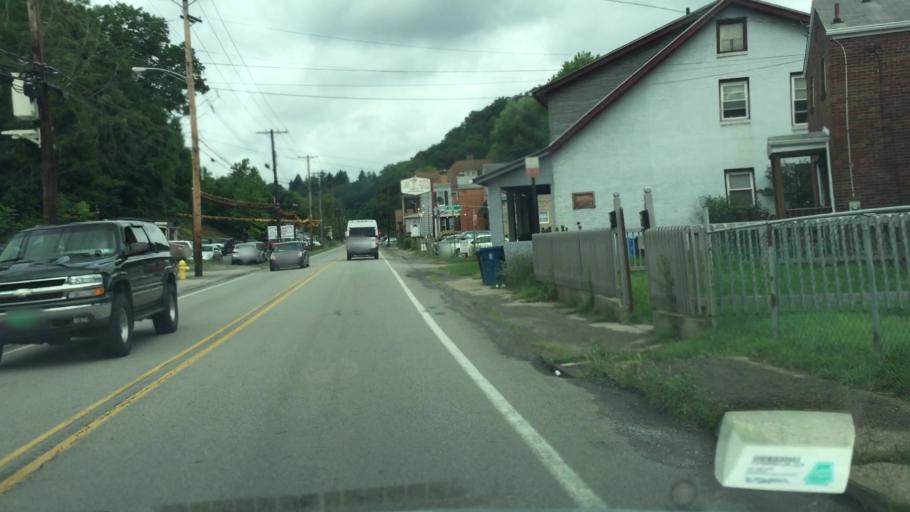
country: US
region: Pennsylvania
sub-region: Allegheny County
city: Millvale
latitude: 40.4972
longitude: -79.9779
